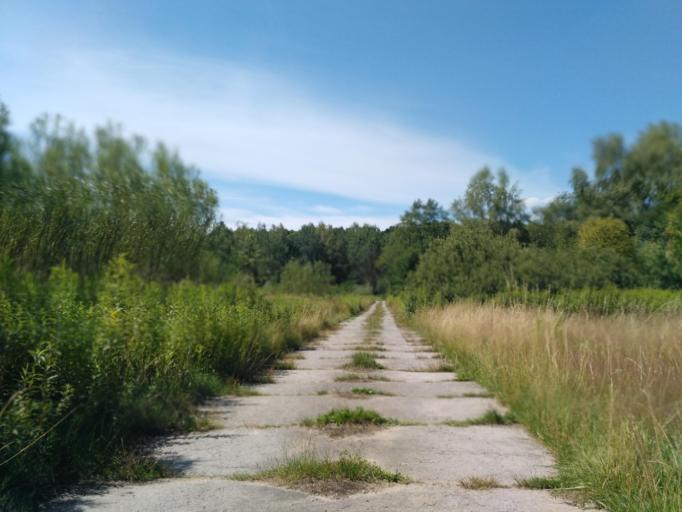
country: PL
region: Subcarpathian Voivodeship
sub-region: Powiat krosnienski
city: Kroscienko Wyzne
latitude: 49.6482
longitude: 21.8527
